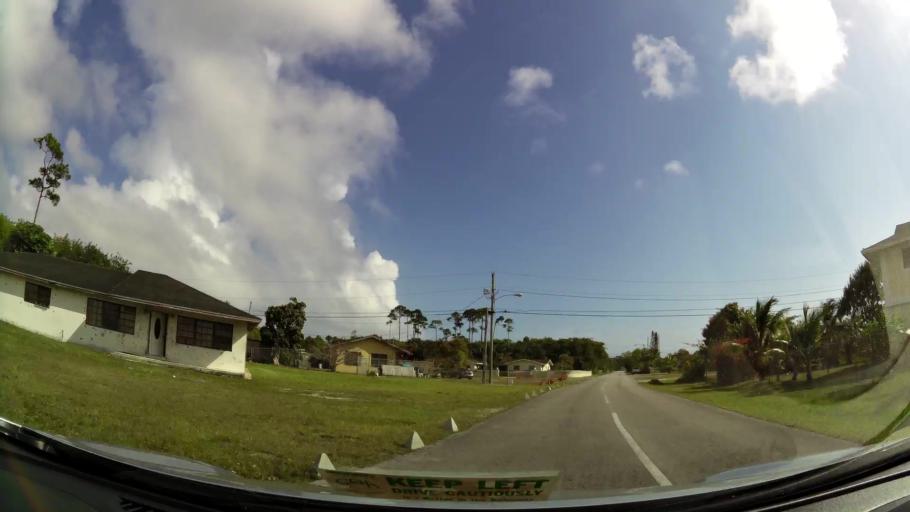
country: BS
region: Freeport
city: Lucaya
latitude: 26.5258
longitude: -78.6762
